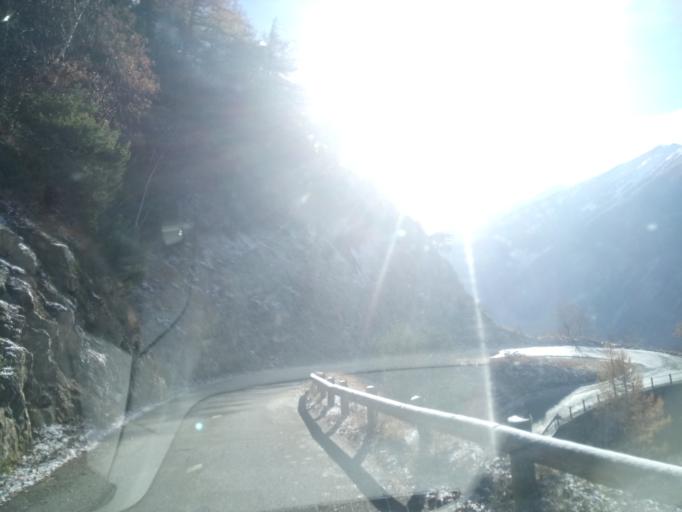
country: FR
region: Rhone-Alpes
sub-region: Departement de la Savoie
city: Villargondran
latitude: 45.2740
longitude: 6.3843
